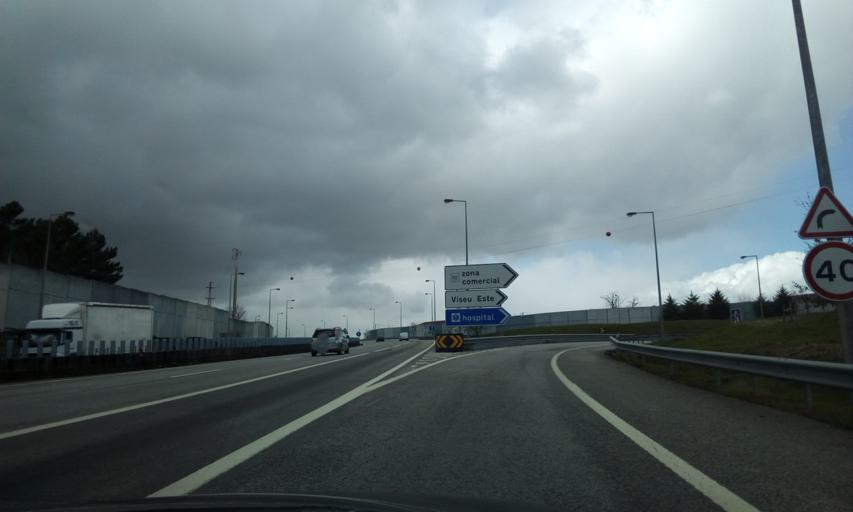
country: PT
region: Viseu
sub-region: Viseu
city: Rio de Loba
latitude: 40.6369
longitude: -7.8485
